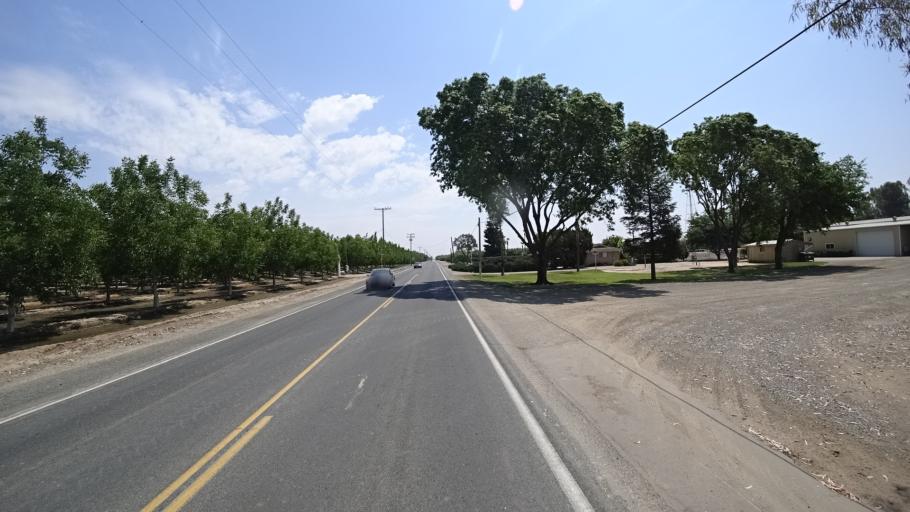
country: US
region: California
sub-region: Kings County
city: Armona
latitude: 36.3280
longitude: -119.7261
